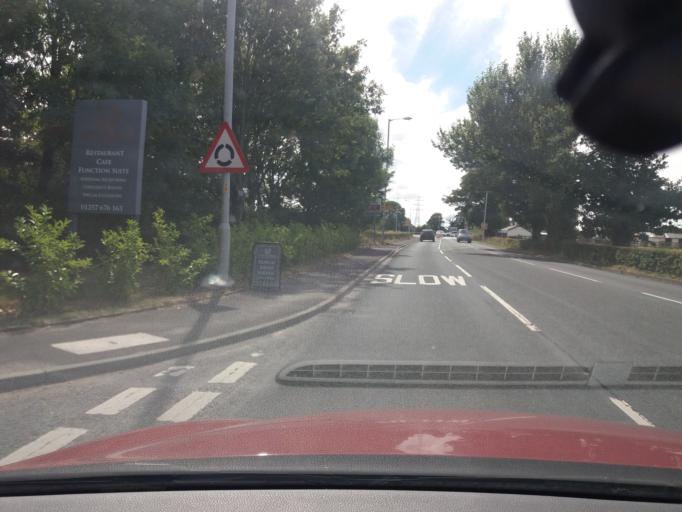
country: GB
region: England
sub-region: Lancashire
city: Coppull
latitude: 53.6306
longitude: -2.6854
